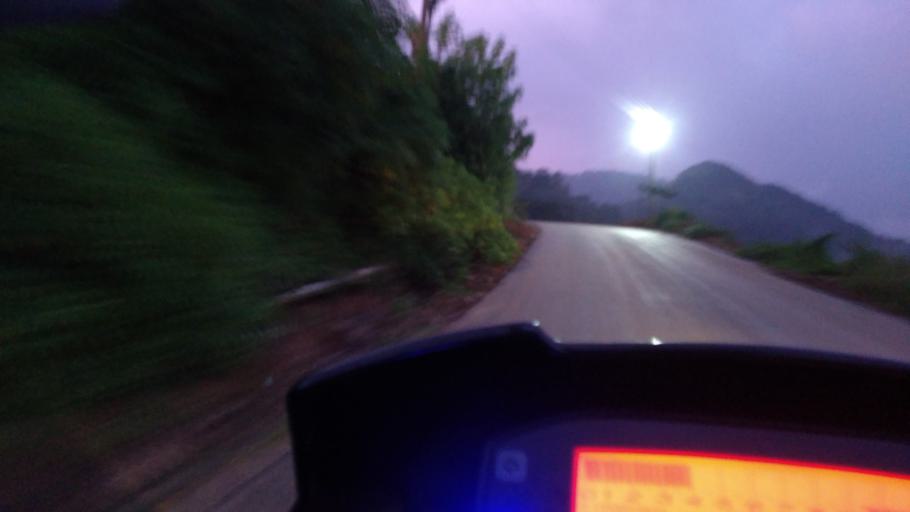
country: IN
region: Kerala
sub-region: Idukki
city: Munnar
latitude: 9.9757
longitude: 77.0580
